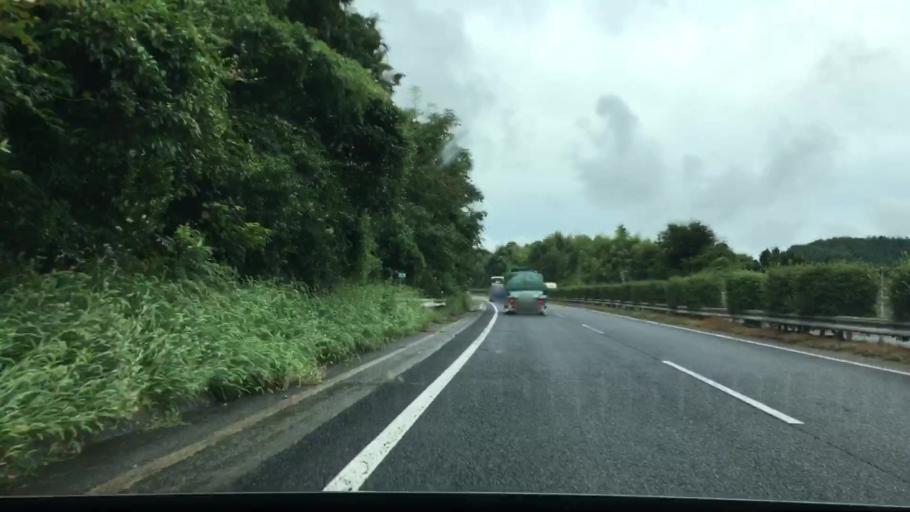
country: JP
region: Hyogo
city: Himeji
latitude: 34.9536
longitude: 134.7371
